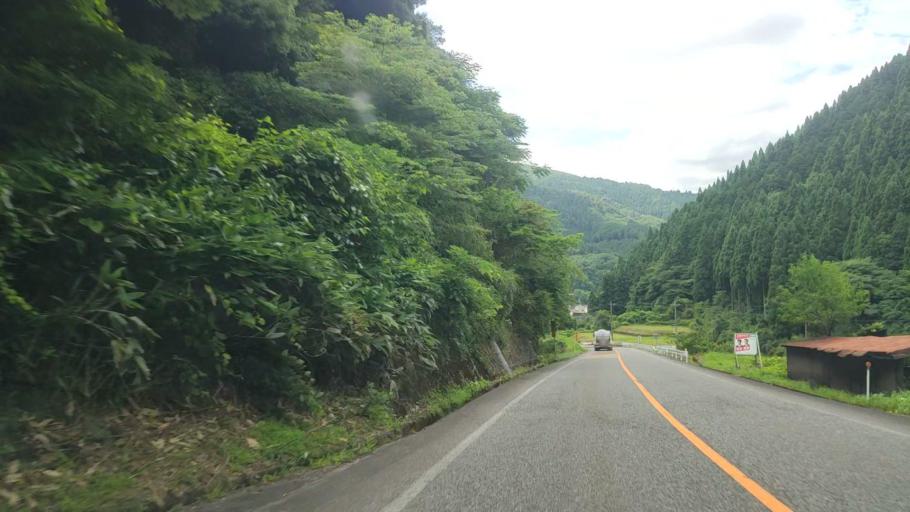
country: JP
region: Tottori
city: Yonago
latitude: 35.2493
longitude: 133.4425
